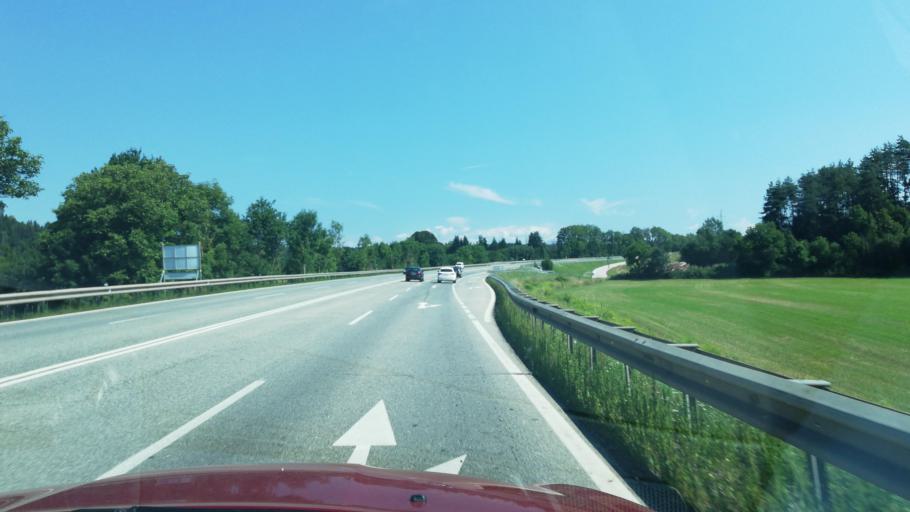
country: AT
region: Carinthia
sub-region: Politischer Bezirk Sankt Veit an der Glan
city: St. Georgen am Laengsee
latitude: 46.7968
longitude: 14.3917
